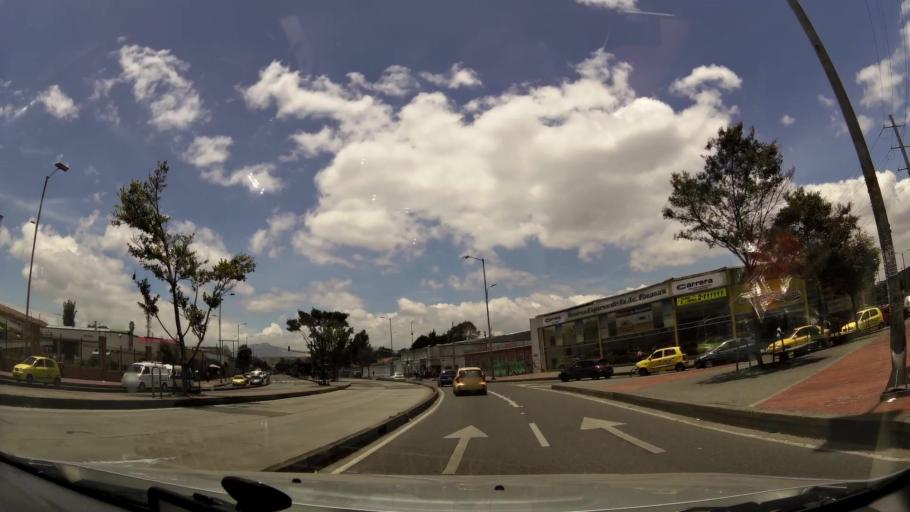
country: CO
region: Bogota D.C.
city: Bogota
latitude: 4.5918
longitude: -74.0894
